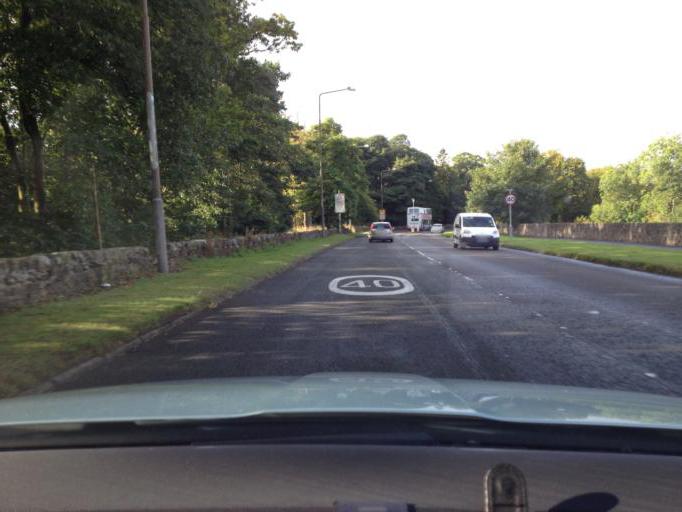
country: GB
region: Scotland
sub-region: West Lothian
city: West Calder
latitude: 55.8645
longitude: -3.5391
